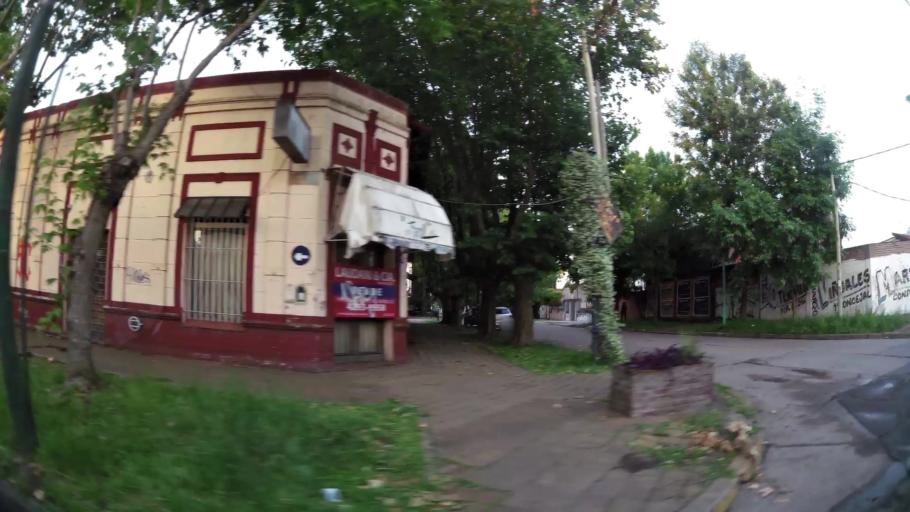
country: AR
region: Buenos Aires
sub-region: Partido de Lomas de Zamora
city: Lomas de Zamora
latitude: -34.7742
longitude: -58.3901
